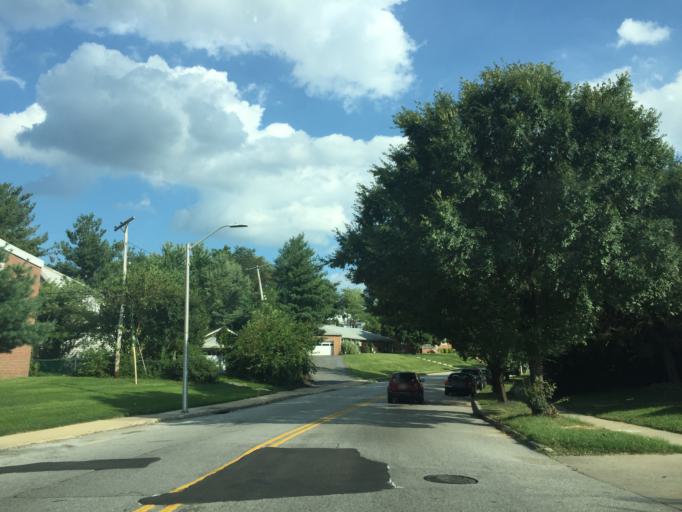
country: US
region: Maryland
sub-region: Baltimore County
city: Parkville
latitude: 39.3422
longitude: -76.5682
